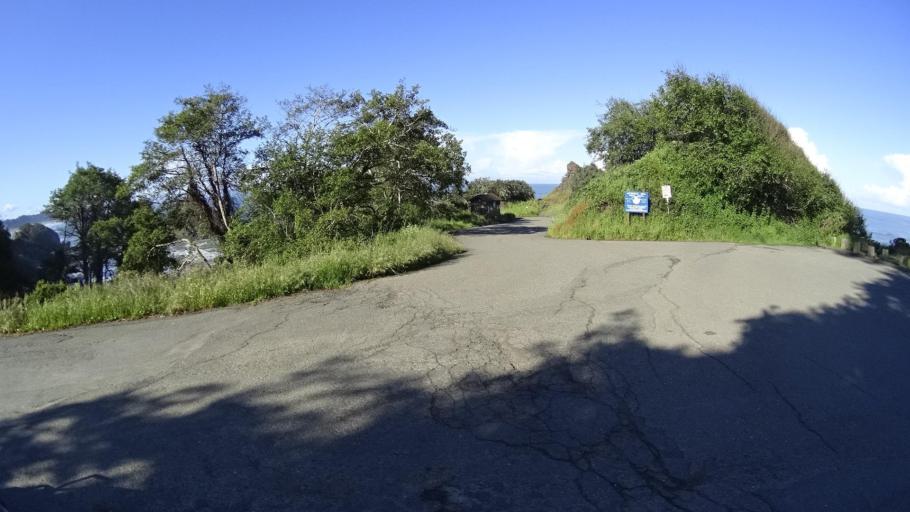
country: US
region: California
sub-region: Humboldt County
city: Westhaven-Moonstone
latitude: 41.0402
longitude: -124.1196
